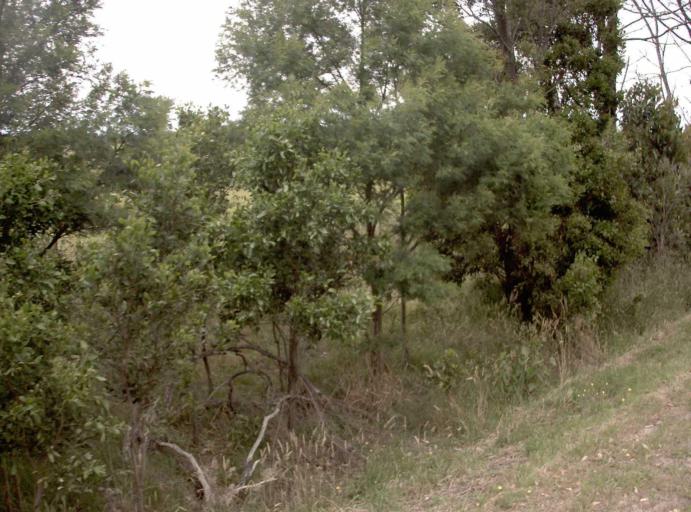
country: AU
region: Victoria
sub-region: Latrobe
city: Traralgon
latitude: -38.4894
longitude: 146.8195
